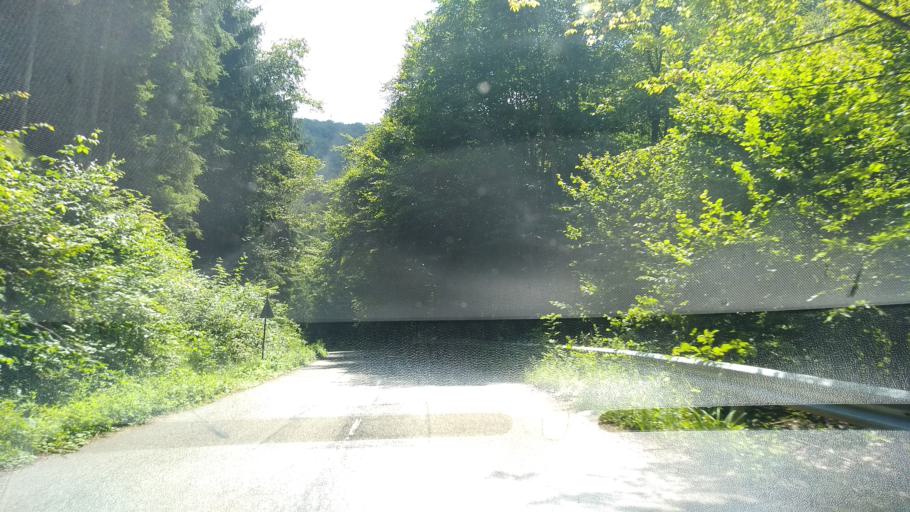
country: RO
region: Hunedoara
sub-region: Comuna Orastioara de Sus
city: Orastioara de Sus
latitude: 45.6464
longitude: 23.1936
